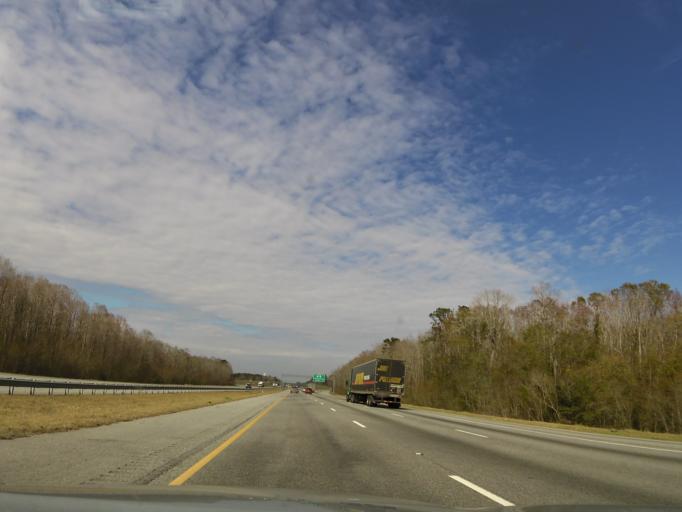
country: US
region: Georgia
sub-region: McIntosh County
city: Darien
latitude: 31.5250
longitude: -81.4453
